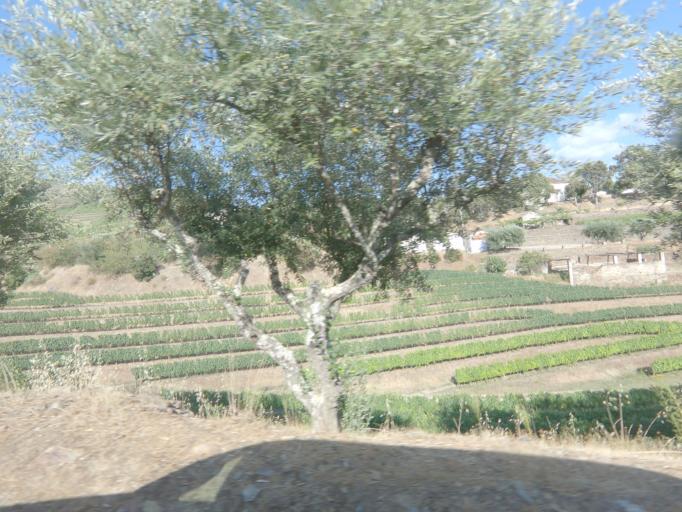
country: PT
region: Viseu
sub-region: Tabuaco
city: Tabuaco
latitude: 41.1867
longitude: -7.5308
